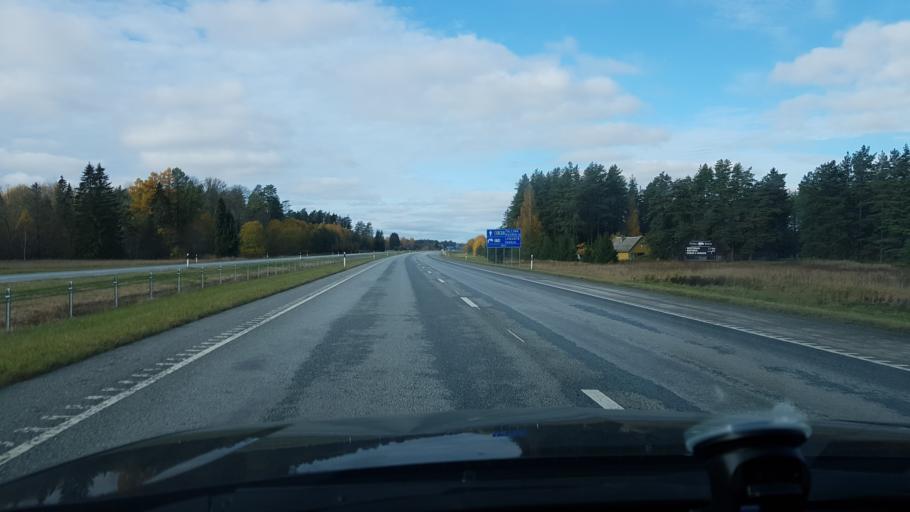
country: EE
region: Laeaene-Virumaa
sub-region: Kadrina vald
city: Kadrina
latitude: 59.4469
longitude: 26.0823
